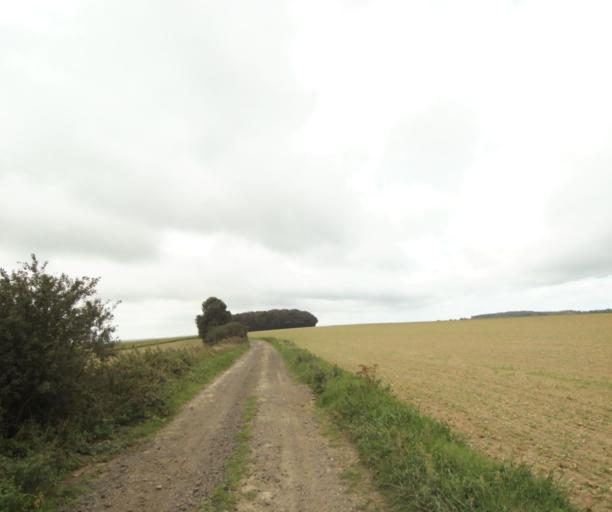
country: FR
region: Nord-Pas-de-Calais
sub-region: Departement du Pas-de-Calais
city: Etaples
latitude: 50.5307
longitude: 1.6718
